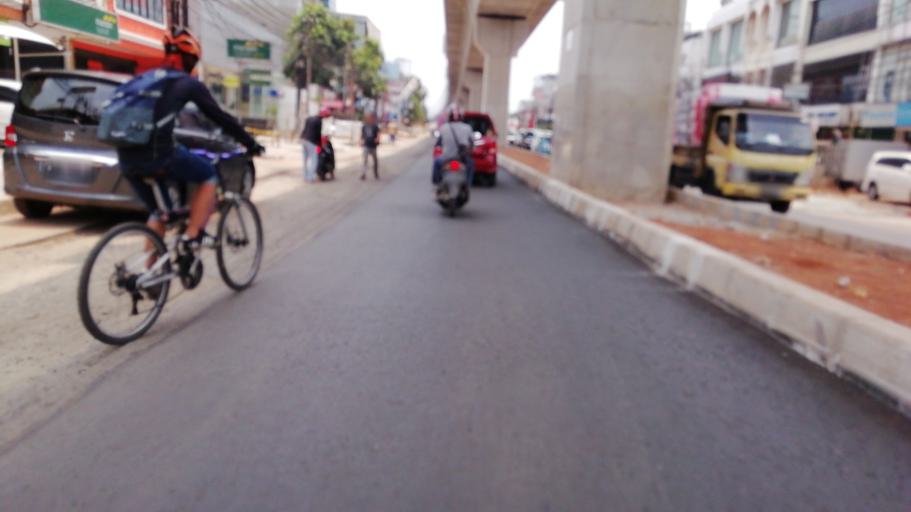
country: ID
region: Jakarta Raya
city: Jakarta
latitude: -6.2756
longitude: 106.7977
